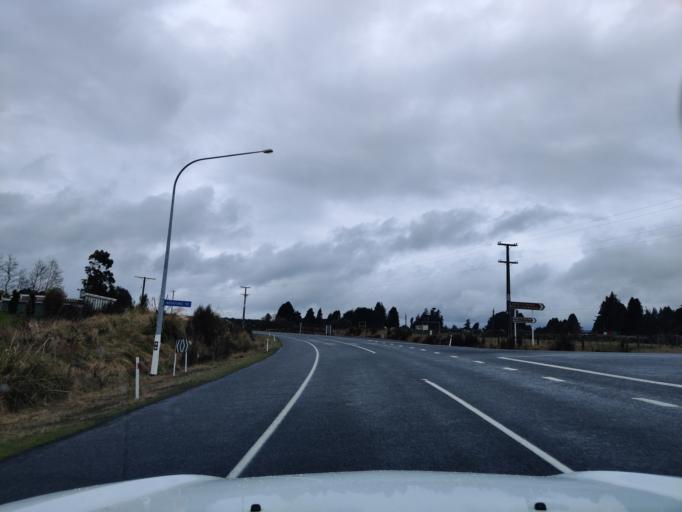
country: NZ
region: Manawatu-Wanganui
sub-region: Ruapehu District
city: Waiouru
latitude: -39.3448
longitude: 175.3760
